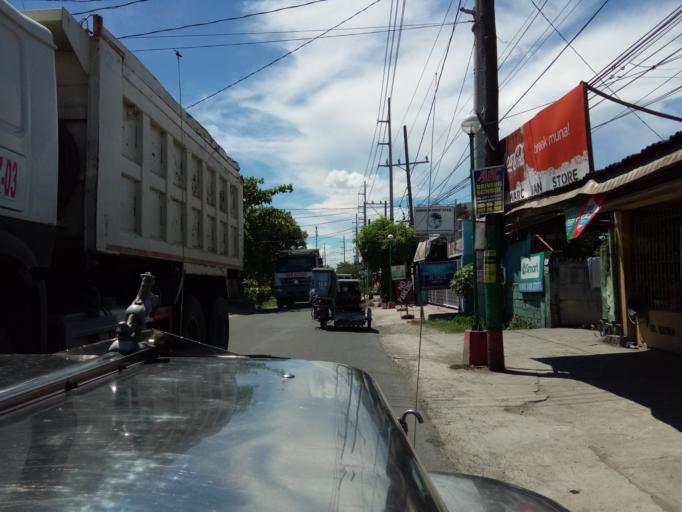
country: PH
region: Calabarzon
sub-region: Province of Cavite
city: Pasong Kawayan Primero
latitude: 14.3642
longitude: 120.8944
